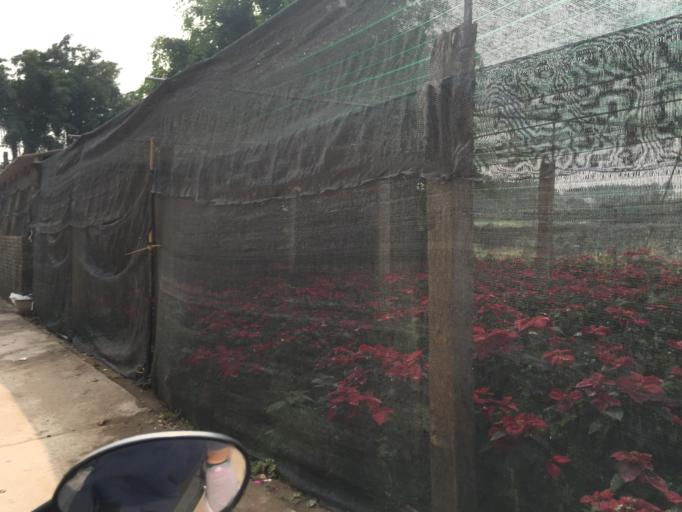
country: VN
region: Hung Yen
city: Van Giang
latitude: 20.9457
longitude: 105.9103
